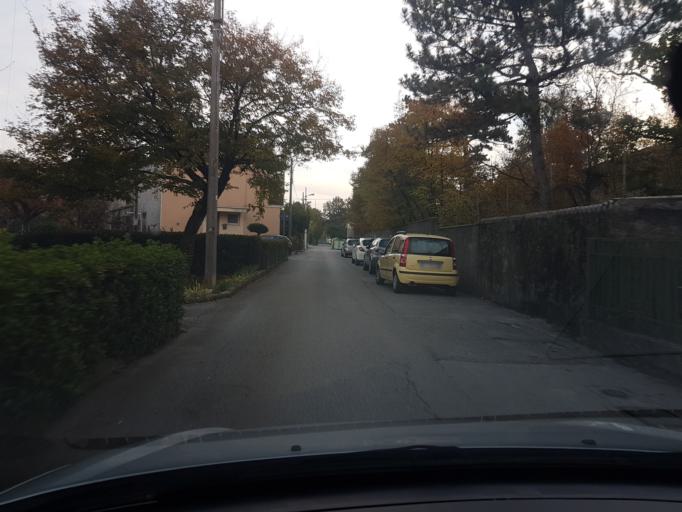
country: IT
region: Friuli Venezia Giulia
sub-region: Provincia di Trieste
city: Sistiana-Visogliano
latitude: 45.7674
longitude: 13.6398
